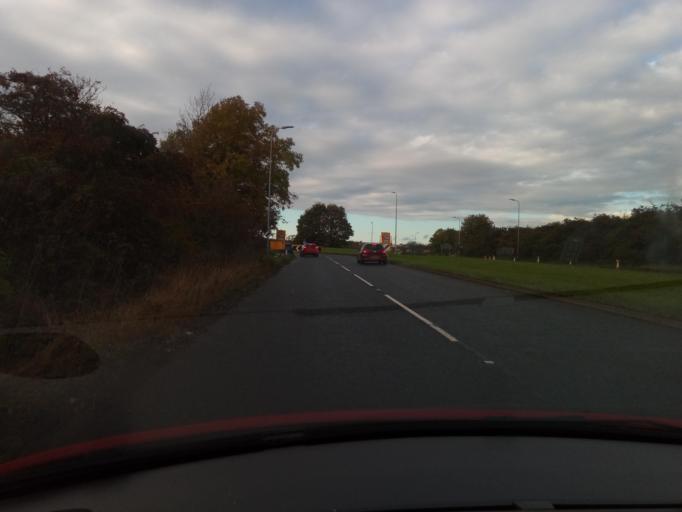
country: GB
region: England
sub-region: Darlington
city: Heighington
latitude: 54.5759
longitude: -1.6124
